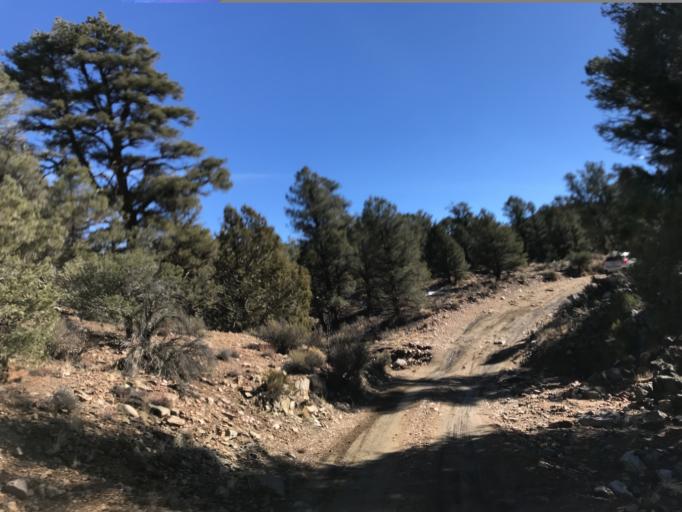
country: US
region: California
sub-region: San Bernardino County
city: Big Bear City
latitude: 34.2533
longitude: -116.7286
